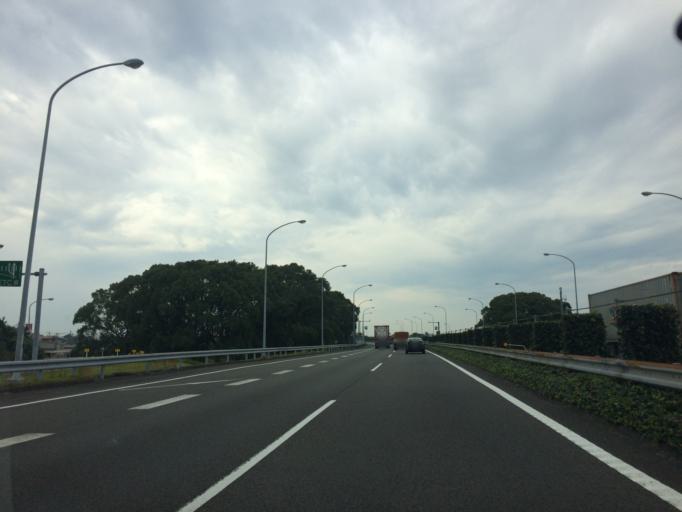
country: JP
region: Shizuoka
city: Yaizu
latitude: 34.8827
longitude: 138.3011
